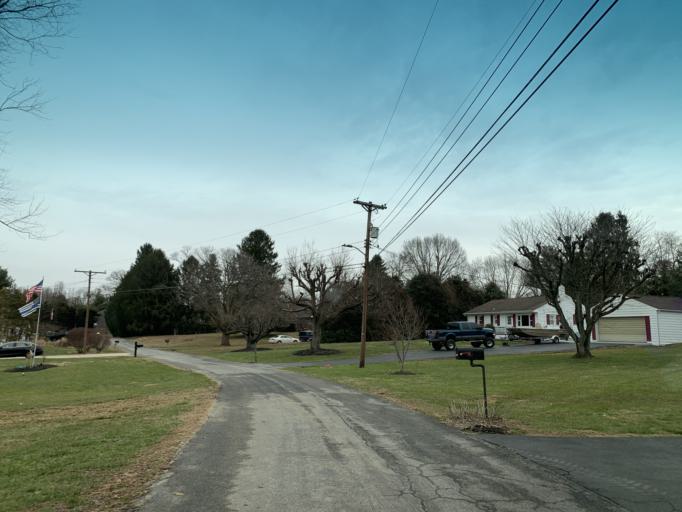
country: US
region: Maryland
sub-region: Harford County
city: South Bel Air
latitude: 39.5539
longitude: -76.2931
